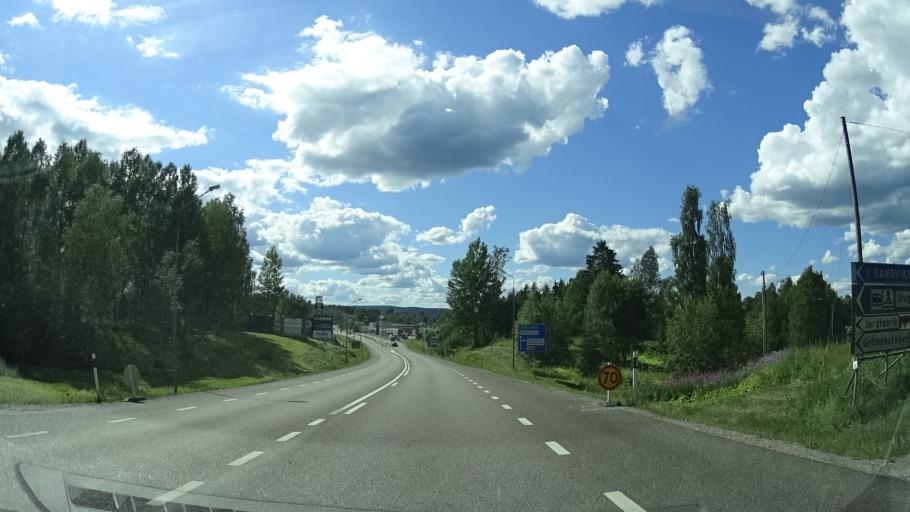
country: SE
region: Vaermland
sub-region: Arjangs Kommun
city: Toecksfors
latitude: 59.5076
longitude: 11.8497
